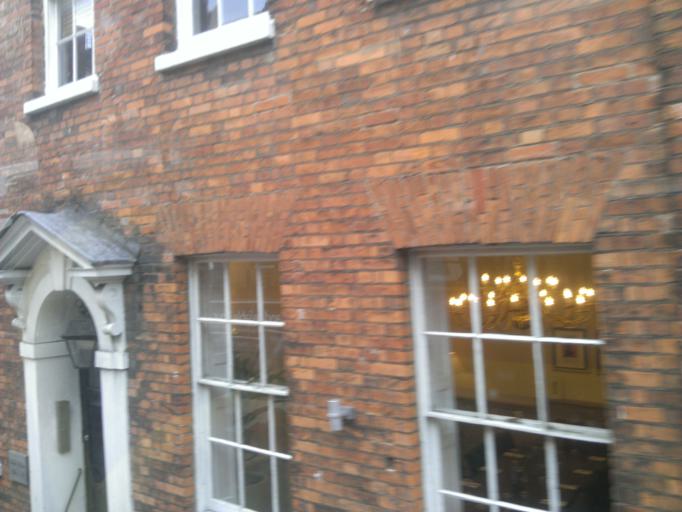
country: GB
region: England
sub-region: Essex
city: Colchester
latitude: 51.8892
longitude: 0.9044
